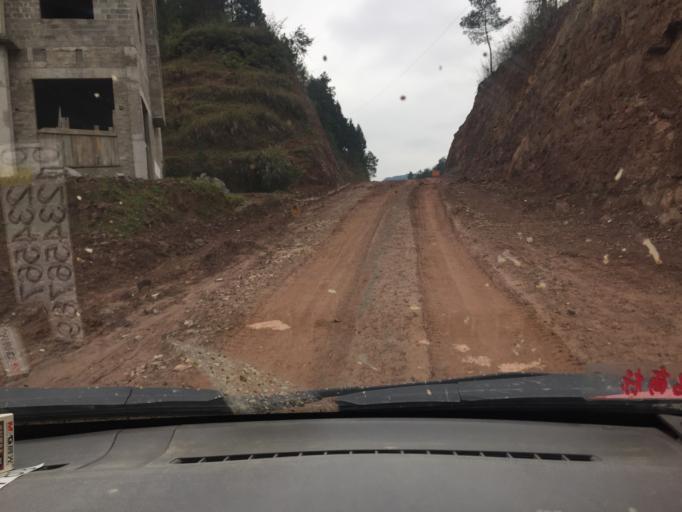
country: CN
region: Guizhou Sheng
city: Fuxing
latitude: 28.0583
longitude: 107.9094
